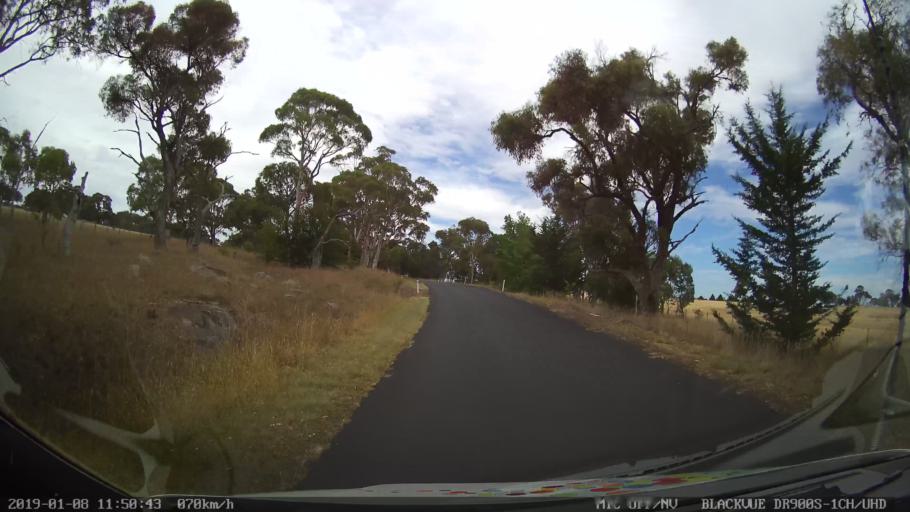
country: AU
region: New South Wales
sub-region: Armidale Dumaresq
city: Armidale
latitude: -30.3858
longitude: 151.5575
